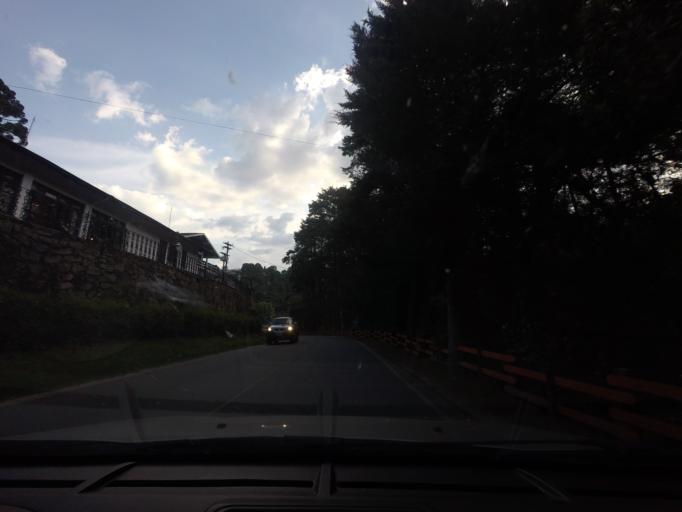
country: BR
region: Sao Paulo
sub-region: Campos Do Jordao
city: Campos do Jordao
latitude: -22.7333
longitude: -45.5709
